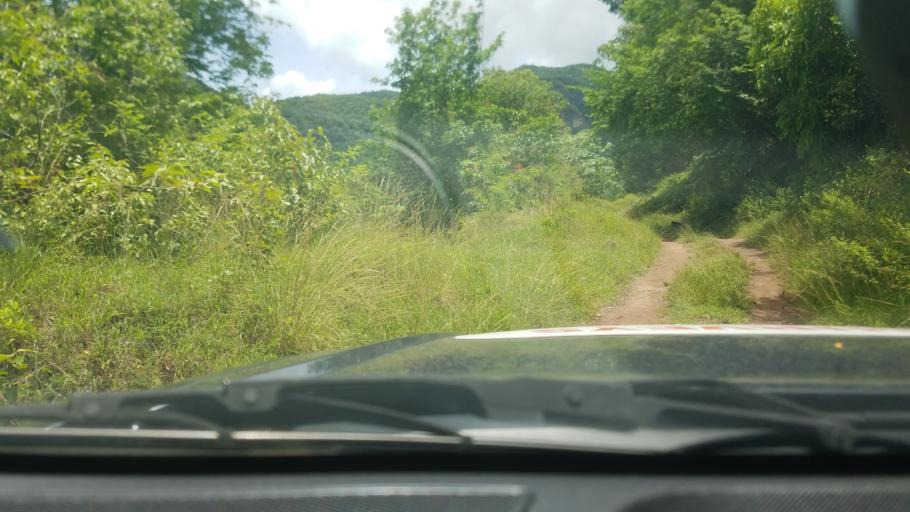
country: LC
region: Soufriere
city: Soufriere
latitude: 13.8475
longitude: -61.0626
